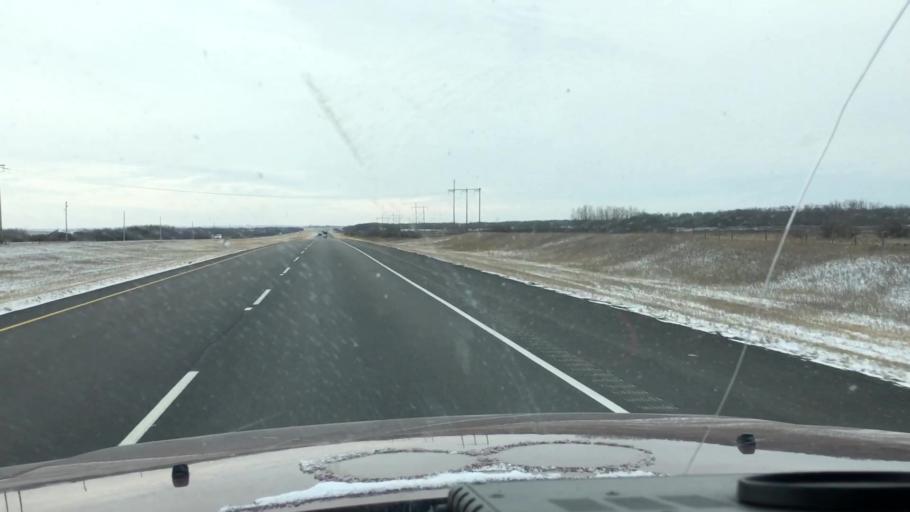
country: CA
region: Saskatchewan
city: Saskatoon
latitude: 51.8933
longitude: -106.5183
